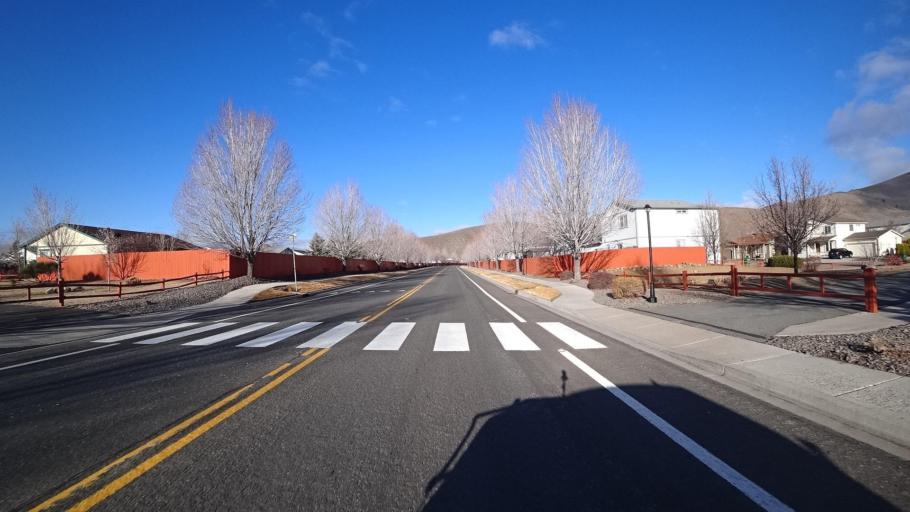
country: US
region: Nevada
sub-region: Washoe County
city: Cold Springs
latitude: 39.6876
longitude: -119.9722
